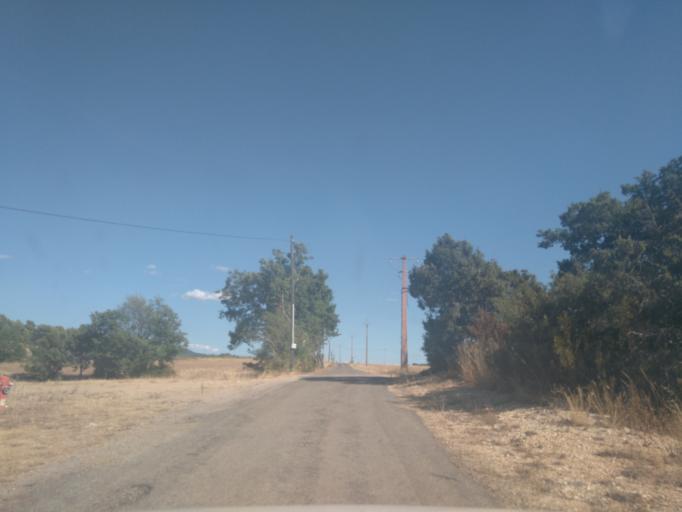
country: FR
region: Provence-Alpes-Cote d'Azur
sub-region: Departement du Var
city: Regusse
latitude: 43.6944
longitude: 6.1139
